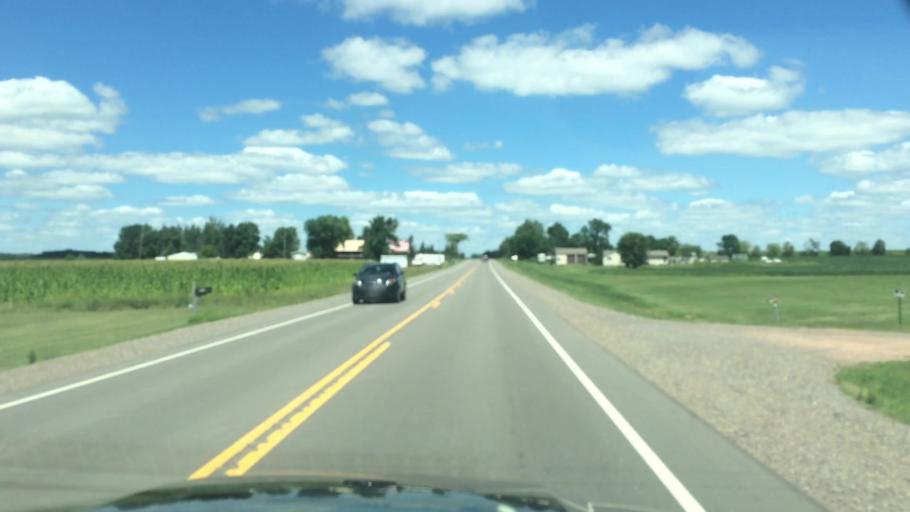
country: US
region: Wisconsin
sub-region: Clark County
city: Abbotsford
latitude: 45.0071
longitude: -90.3155
